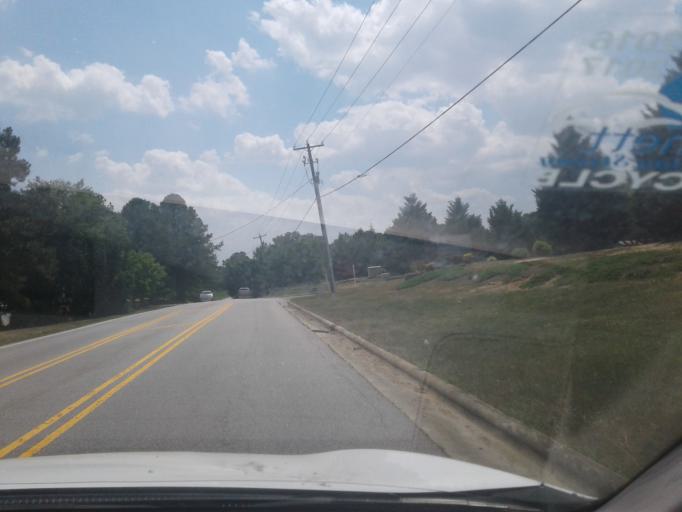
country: US
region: North Carolina
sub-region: Johnston County
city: Benson
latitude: 35.4042
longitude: -78.5411
